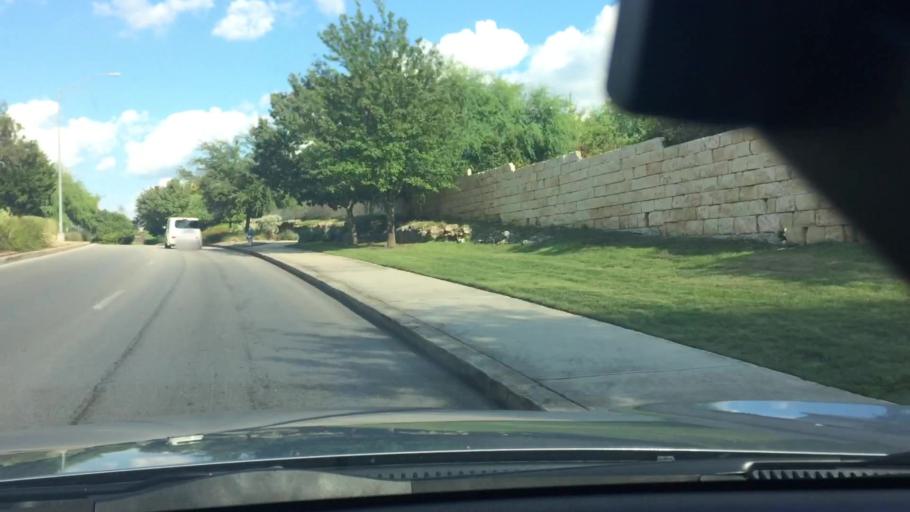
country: US
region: Texas
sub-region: Bexar County
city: Timberwood Park
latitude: 29.6604
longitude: -98.4285
